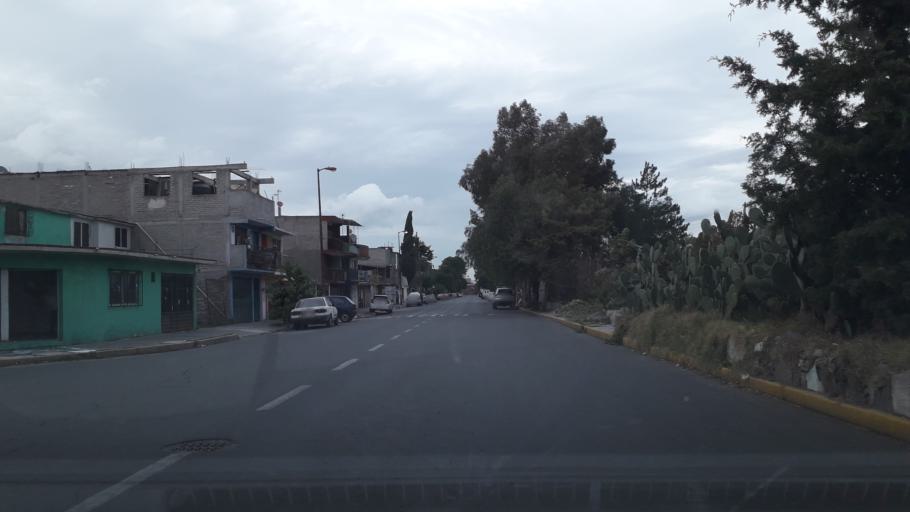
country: MX
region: Mexico
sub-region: Jaltenco
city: Alborada Jaltenco
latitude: 19.6623
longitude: -99.0653
